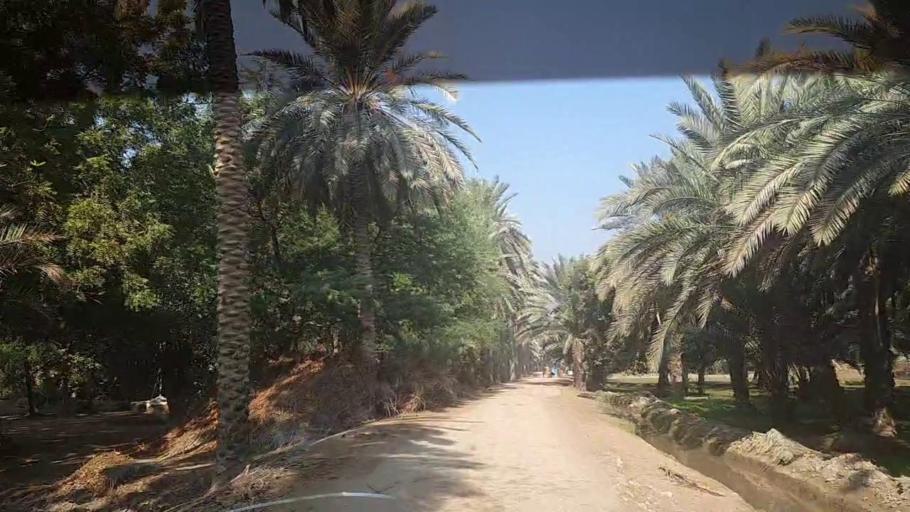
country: PK
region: Sindh
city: Khairpur
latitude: 27.4636
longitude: 68.7175
